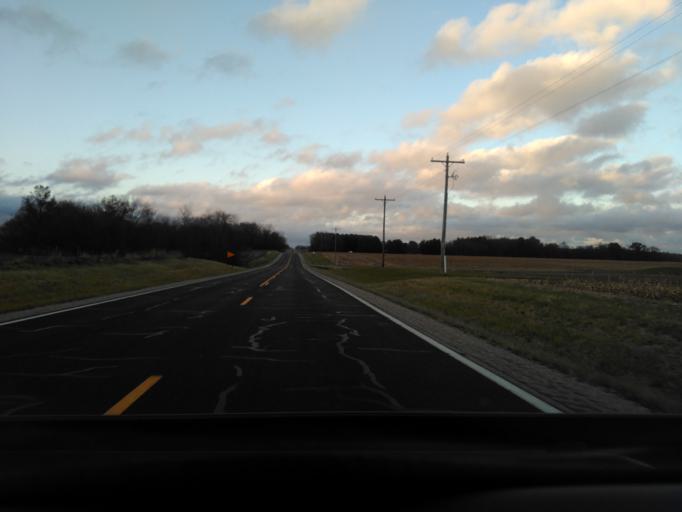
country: US
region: Illinois
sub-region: Effingham County
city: Altamont
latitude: 38.9614
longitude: -88.7490
